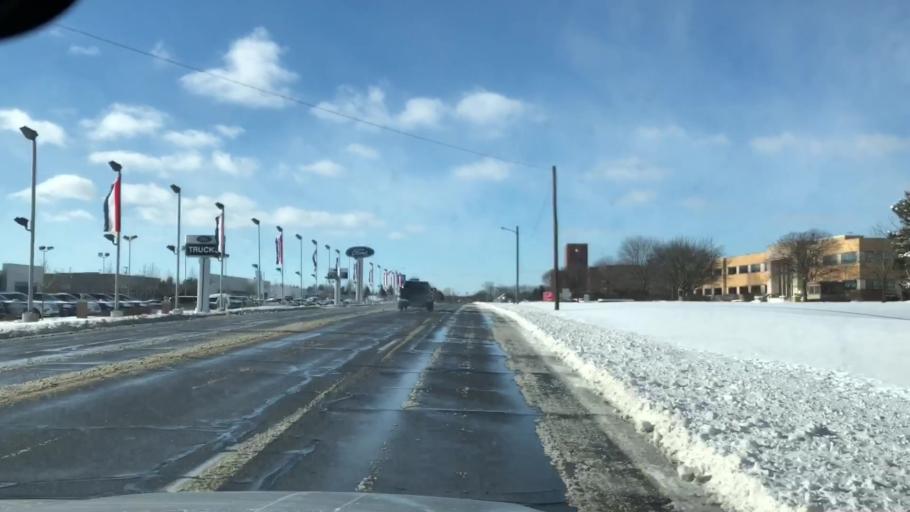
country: US
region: Michigan
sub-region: Wayne County
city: Plymouth
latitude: 42.3737
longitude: -83.4404
